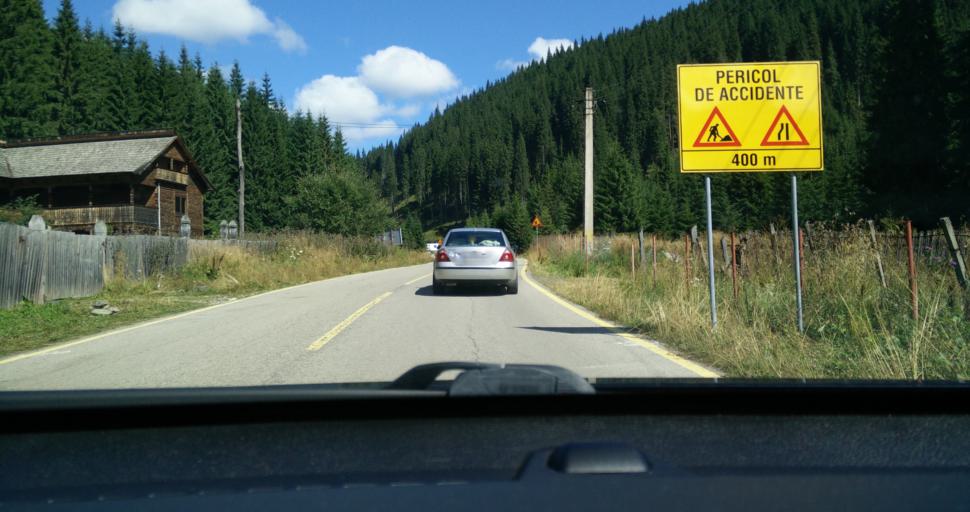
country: RO
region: Hunedoara
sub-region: Oras Petrila
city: Petrila
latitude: 45.4363
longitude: 23.6299
